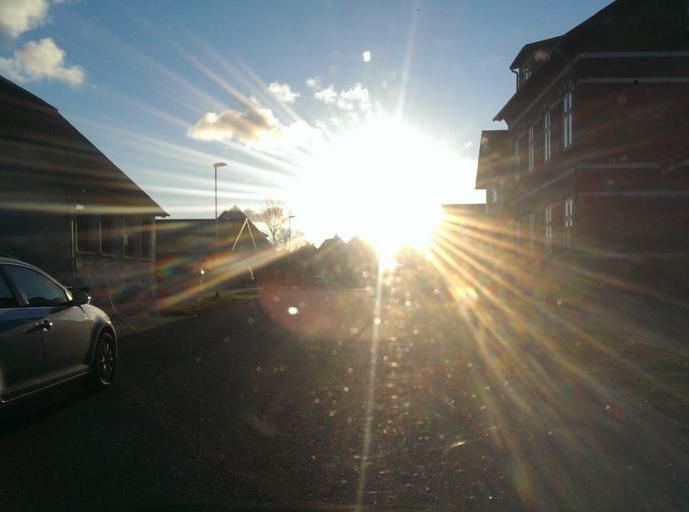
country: DK
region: South Denmark
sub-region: Esbjerg Kommune
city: Esbjerg
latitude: 55.4742
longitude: 8.4849
